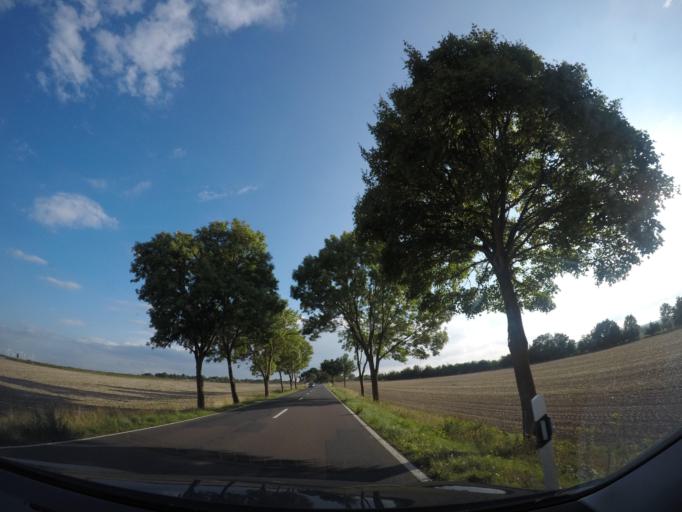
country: DE
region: Saxony-Anhalt
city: Weferlingen
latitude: 52.3551
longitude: 11.0788
